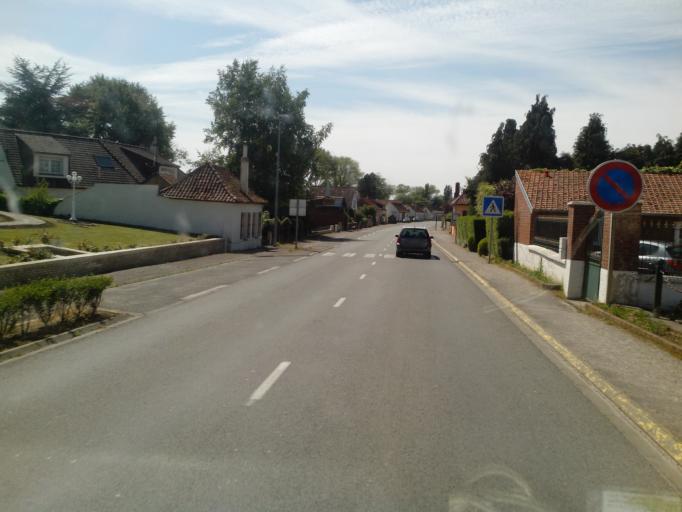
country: FR
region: Nord-Pas-de-Calais
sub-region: Departement du Pas-de-Calais
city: Montreuil
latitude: 50.4908
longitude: 1.7275
